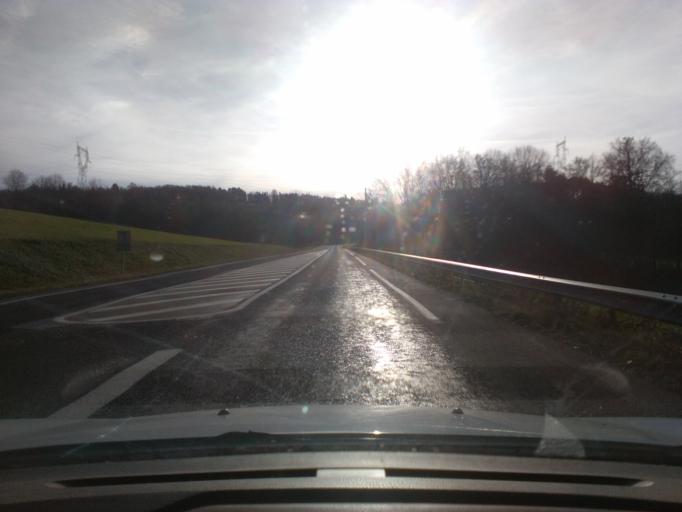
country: FR
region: Lorraine
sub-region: Departement des Vosges
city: Anould
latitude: 48.1735
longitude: 6.9276
